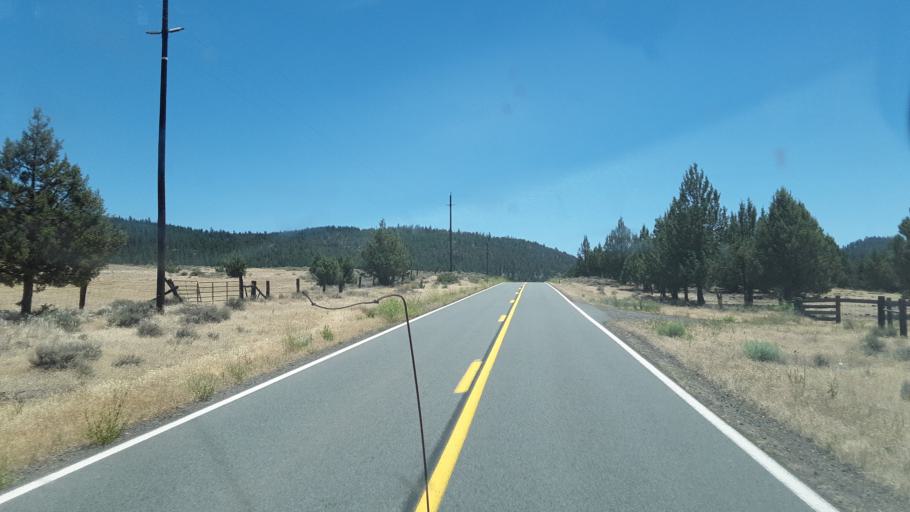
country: US
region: California
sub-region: Modoc County
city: Alturas
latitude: 41.0442
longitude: -120.8646
